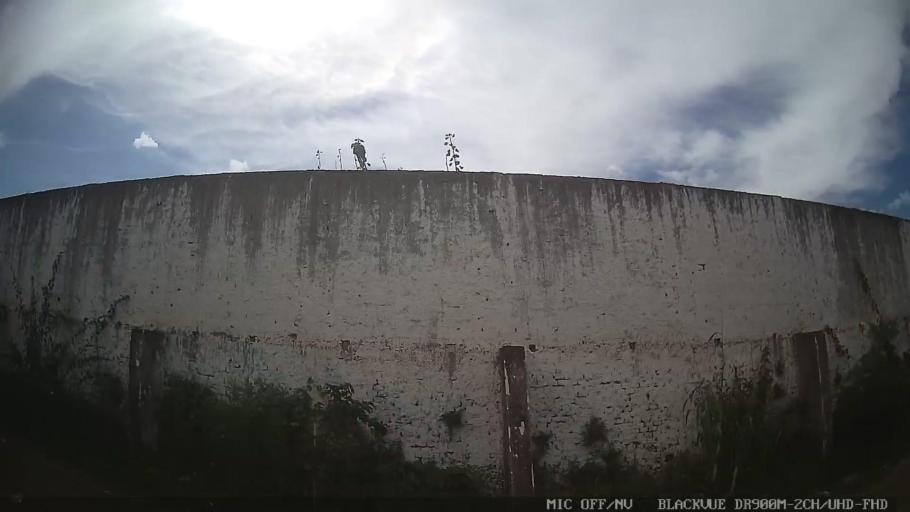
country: BR
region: Sao Paulo
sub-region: Conchas
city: Conchas
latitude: -23.0096
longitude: -48.0044
